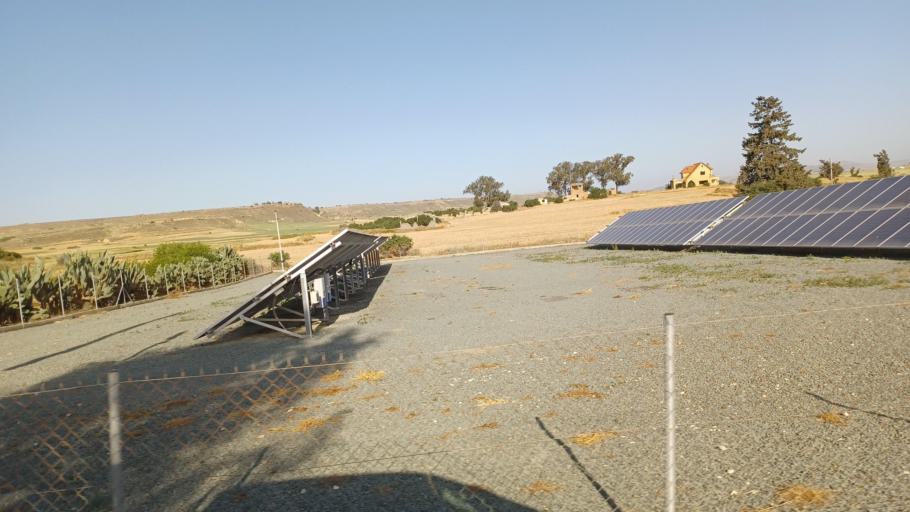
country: CY
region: Lefkosia
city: Mammari
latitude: 35.1670
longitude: 33.2489
